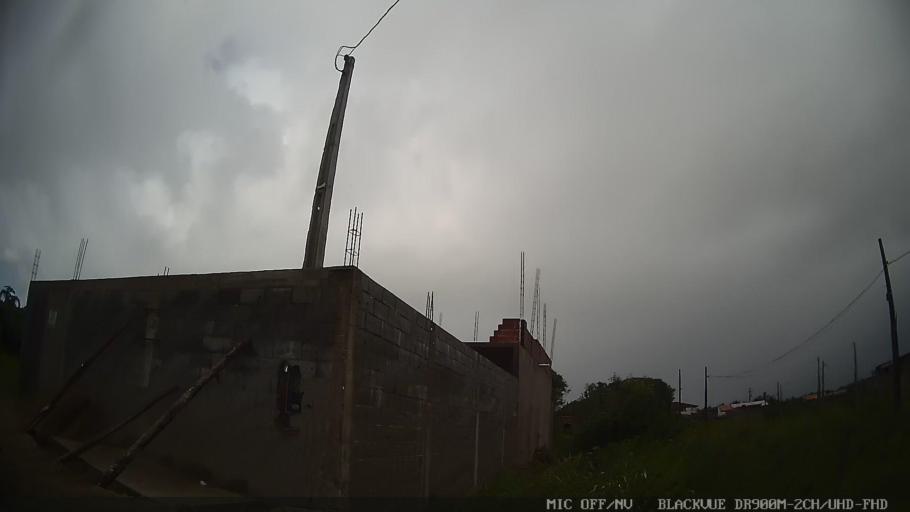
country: BR
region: Sao Paulo
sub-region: Peruibe
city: Peruibe
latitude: -24.2509
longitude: -46.8988
